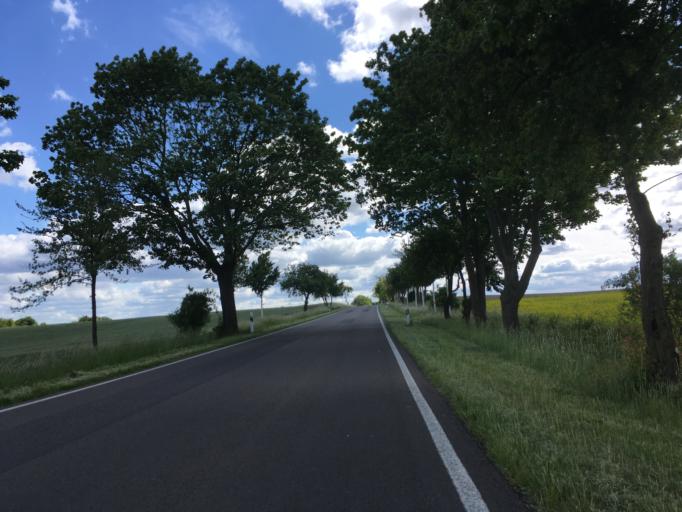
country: DE
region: Brandenburg
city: Protzel
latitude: 52.6527
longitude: 13.9891
